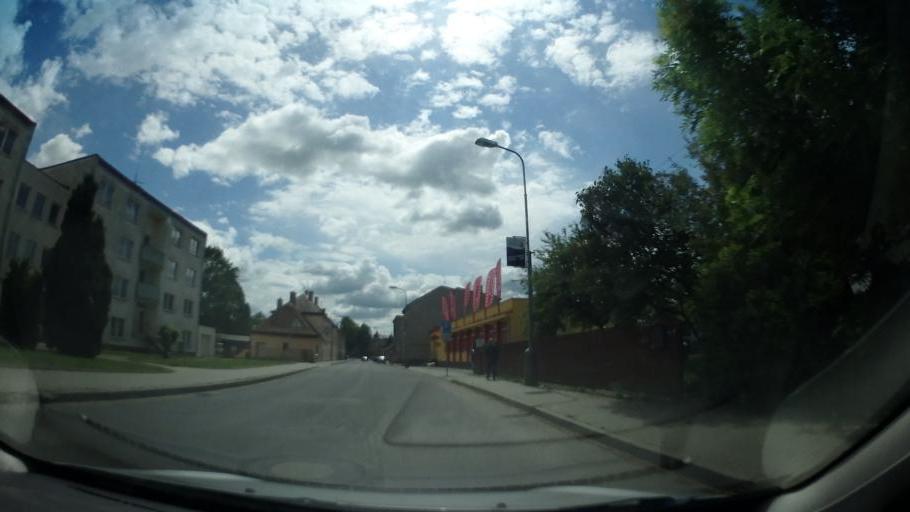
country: CZ
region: Pardubicky
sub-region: Okres Svitavy
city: Moravska Trebova
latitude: 49.7549
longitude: 16.6595
